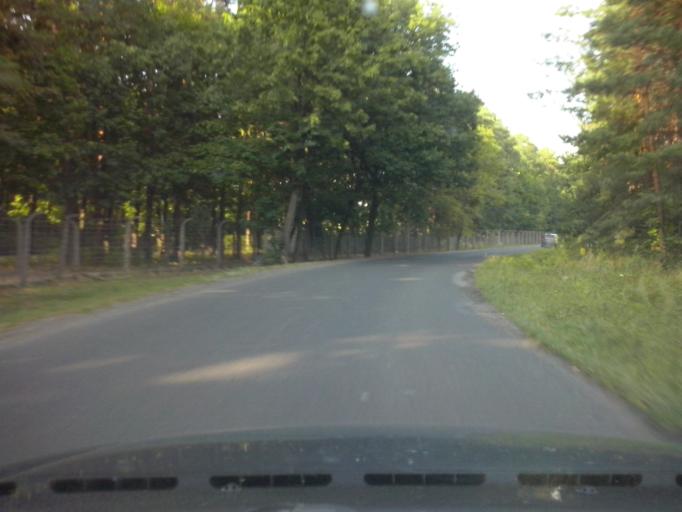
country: PL
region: Subcarpathian Voivodeship
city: Nowa Sarzyna
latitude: 50.3245
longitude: 22.3329
